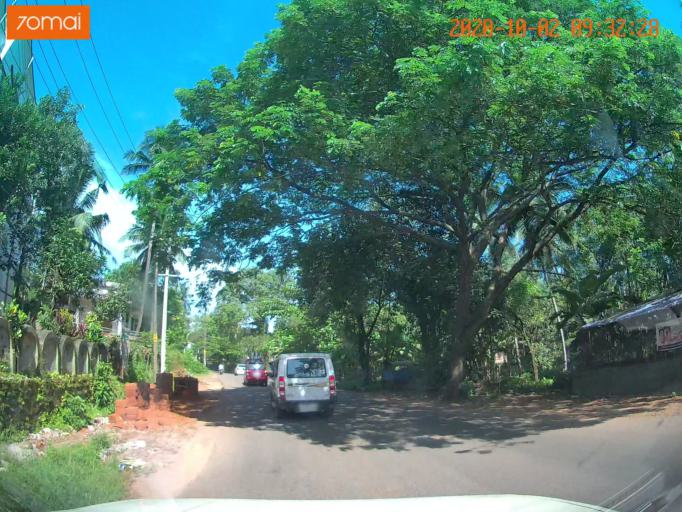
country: IN
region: Kerala
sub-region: Kozhikode
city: Nadapuram
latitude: 11.6277
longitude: 75.7565
